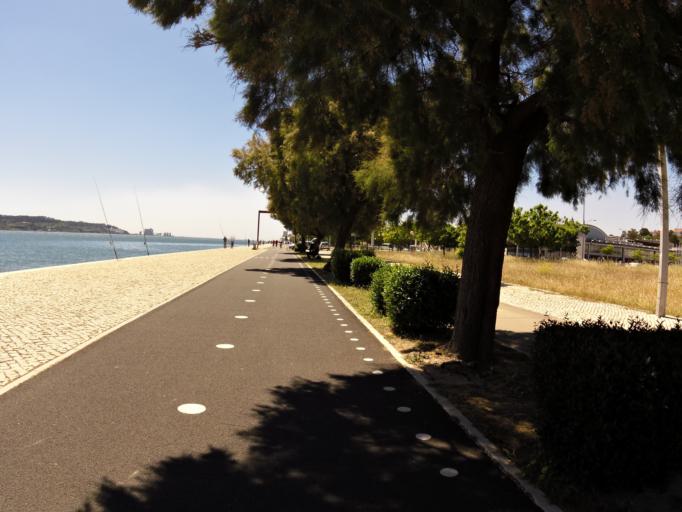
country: PT
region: Setubal
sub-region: Almada
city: Pragal
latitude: 38.6980
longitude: -9.1813
